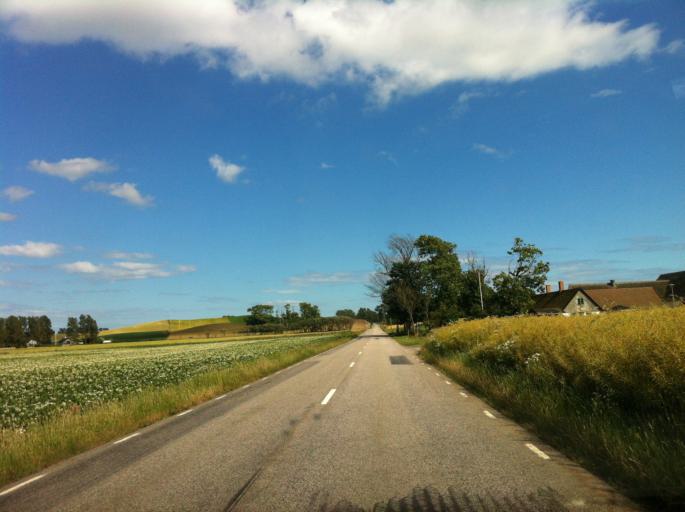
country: SE
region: Skane
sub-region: Ystads Kommun
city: Kopingebro
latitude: 55.4205
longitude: 13.9938
